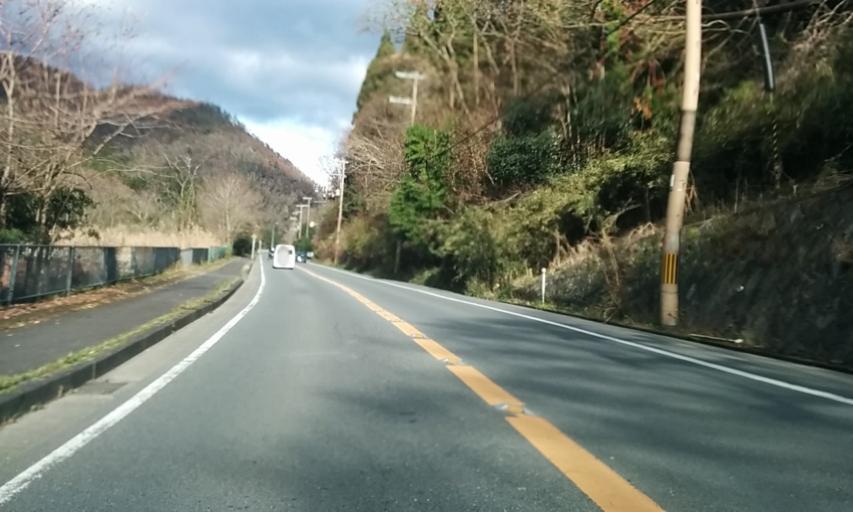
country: JP
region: Kyoto
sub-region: Kyoto-shi
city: Kamigyo-ku
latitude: 35.0703
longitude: 135.8113
